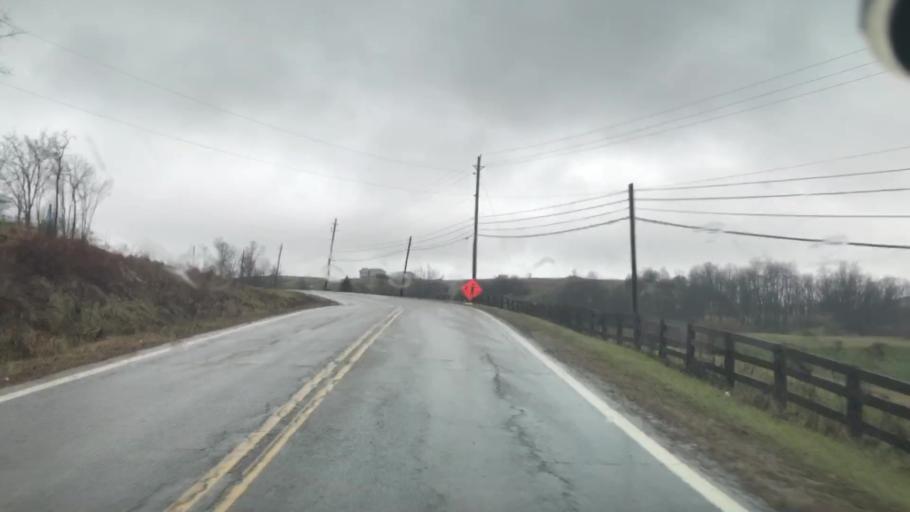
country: US
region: Ohio
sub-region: Harrison County
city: Cadiz
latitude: 40.2496
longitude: -81.0025
